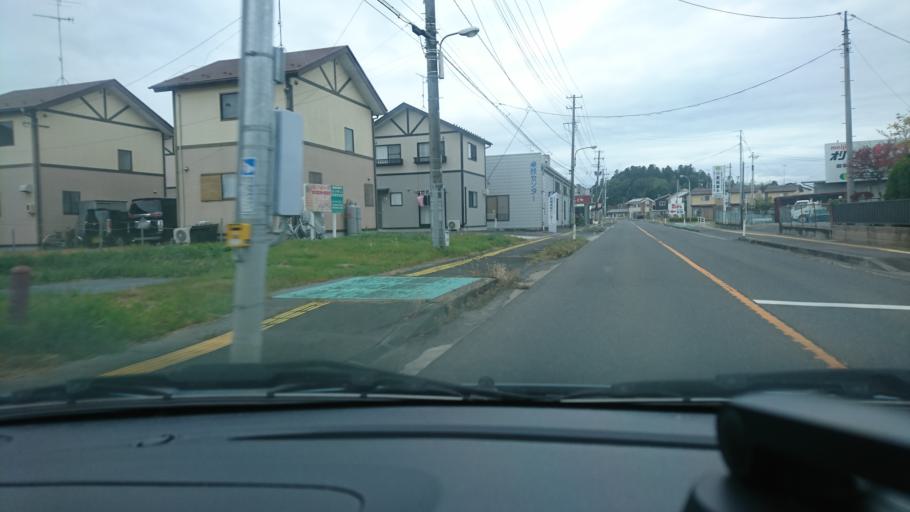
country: JP
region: Iwate
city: Ichinoseki
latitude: 38.7716
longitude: 141.1248
